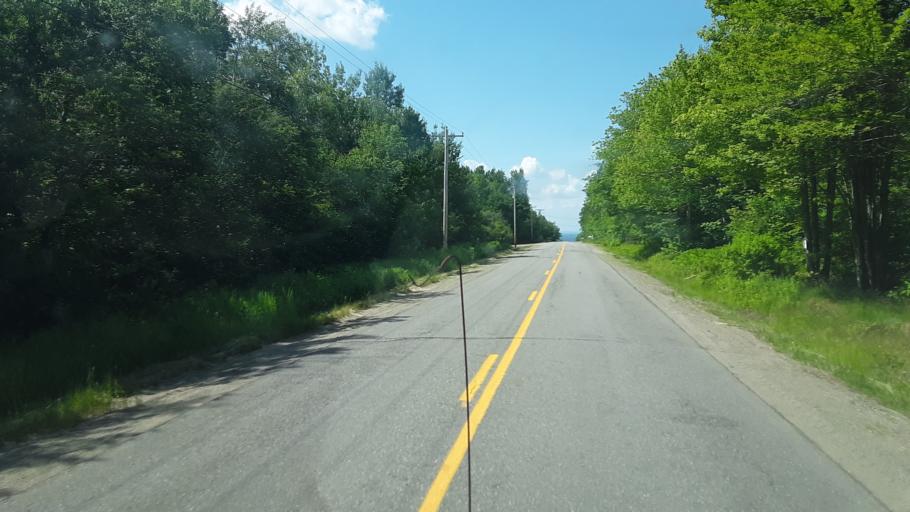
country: US
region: Maine
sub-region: Washington County
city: Calais
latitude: 45.0903
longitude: -67.5048
